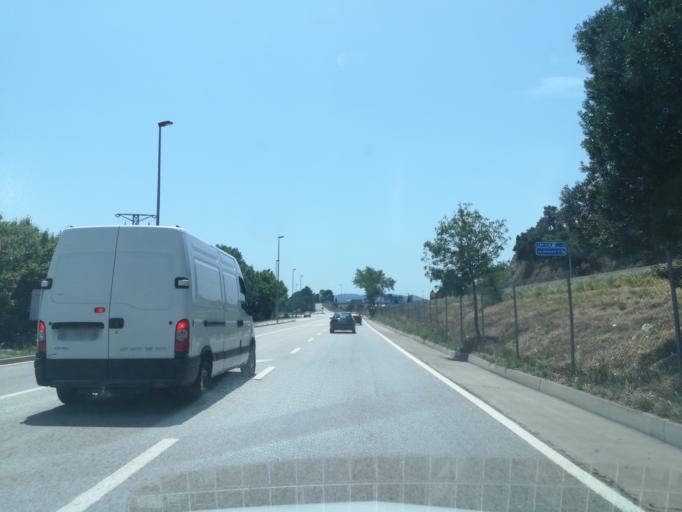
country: ES
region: Catalonia
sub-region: Provincia de Girona
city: la Jonquera
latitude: 42.4166
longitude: 2.8717
